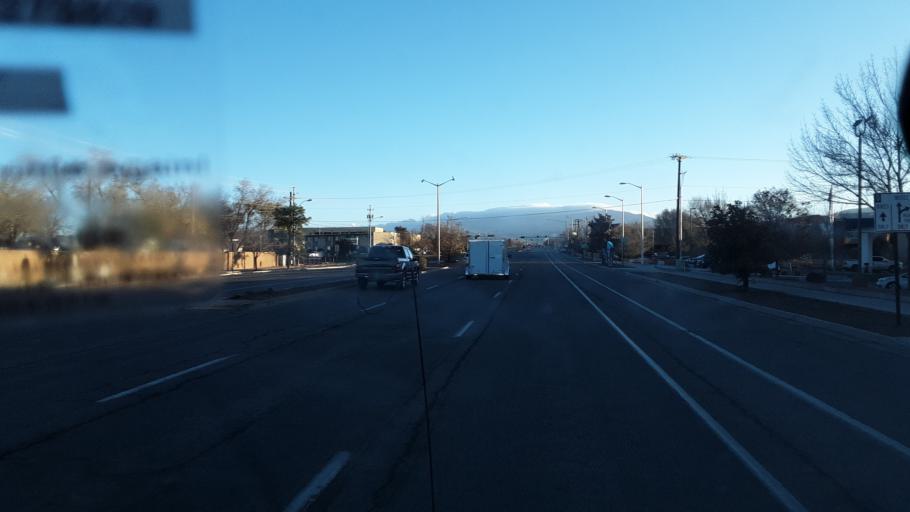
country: US
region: New Mexico
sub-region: Santa Fe County
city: Agua Fria
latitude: 35.6467
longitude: -106.0055
